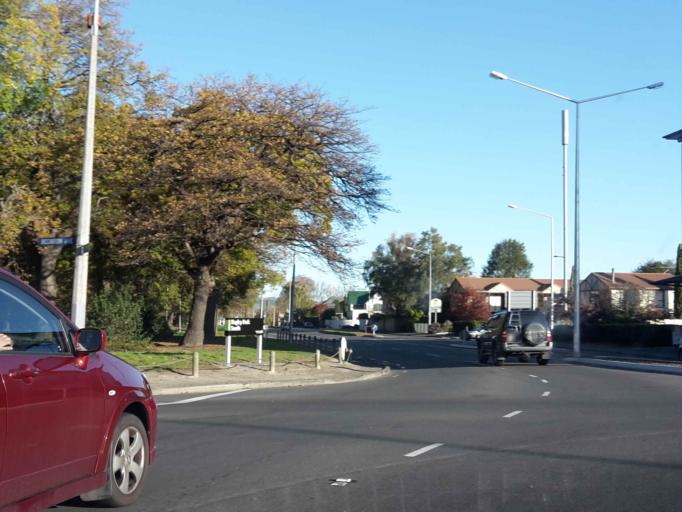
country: NZ
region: Canterbury
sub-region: Christchurch City
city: Christchurch
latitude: -43.5288
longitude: 172.6124
